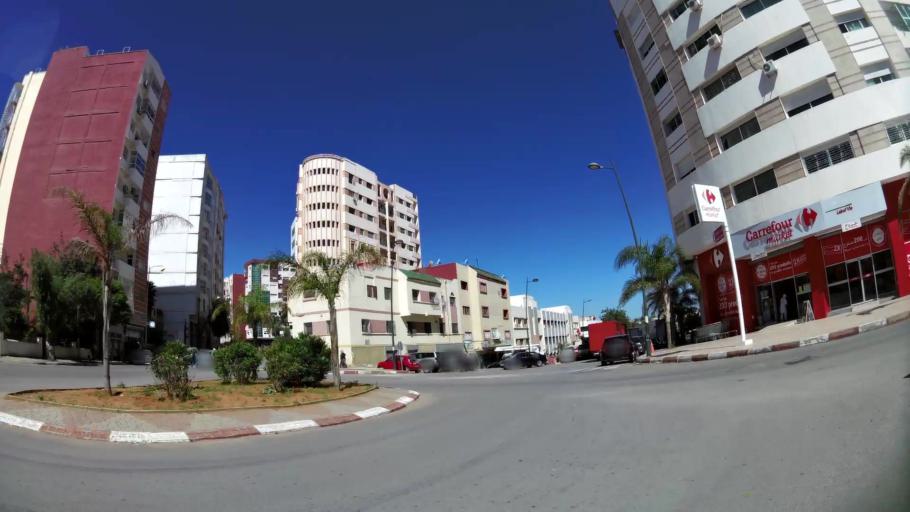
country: MA
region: Meknes-Tafilalet
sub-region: Meknes
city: Meknes
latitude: 33.9022
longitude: -5.5460
